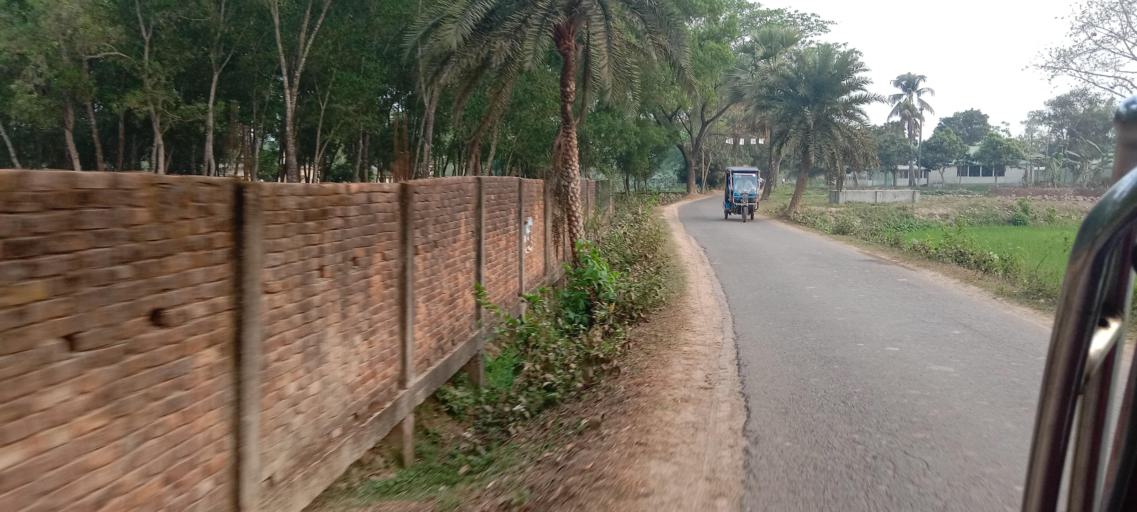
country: BD
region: Dhaka
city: Sakhipur
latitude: 24.4375
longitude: 90.2626
